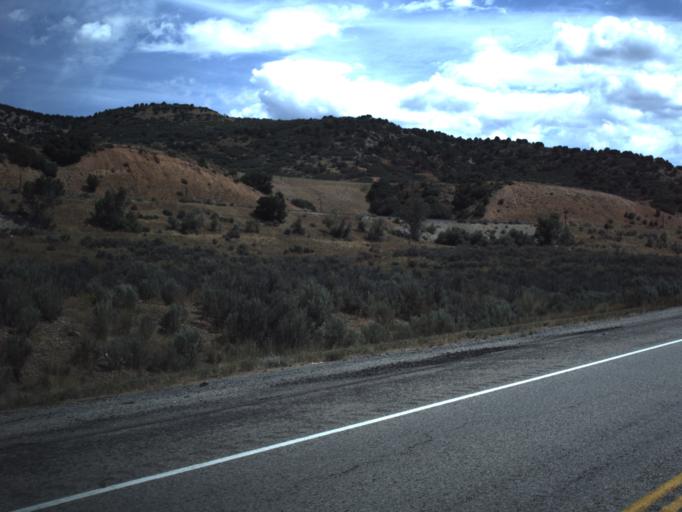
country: US
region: Utah
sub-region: Utah County
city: Mapleton
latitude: 39.9963
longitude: -111.4824
